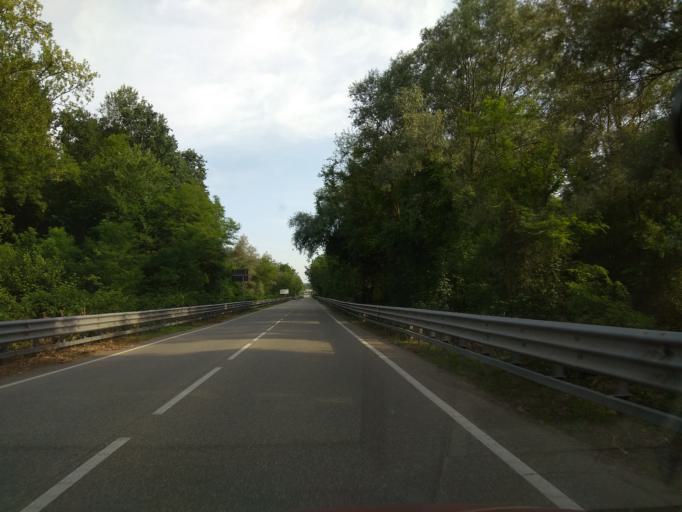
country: IT
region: Piedmont
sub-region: Provincia di Biella
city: Quaregna
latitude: 45.5740
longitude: 8.1689
